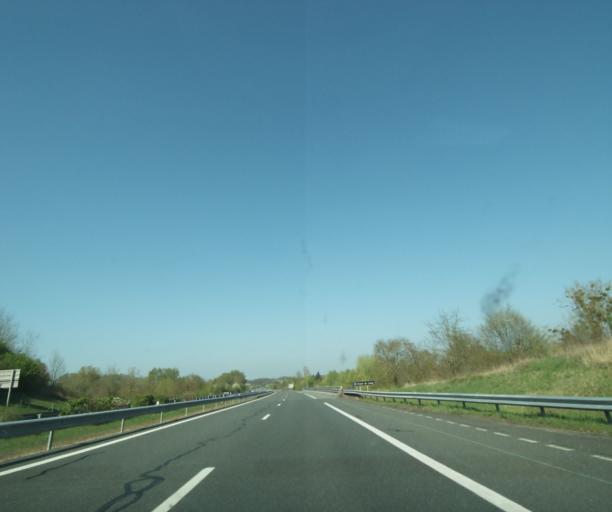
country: FR
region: Centre
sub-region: Departement du Loiret
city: Dordives
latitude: 48.1491
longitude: 2.7500
